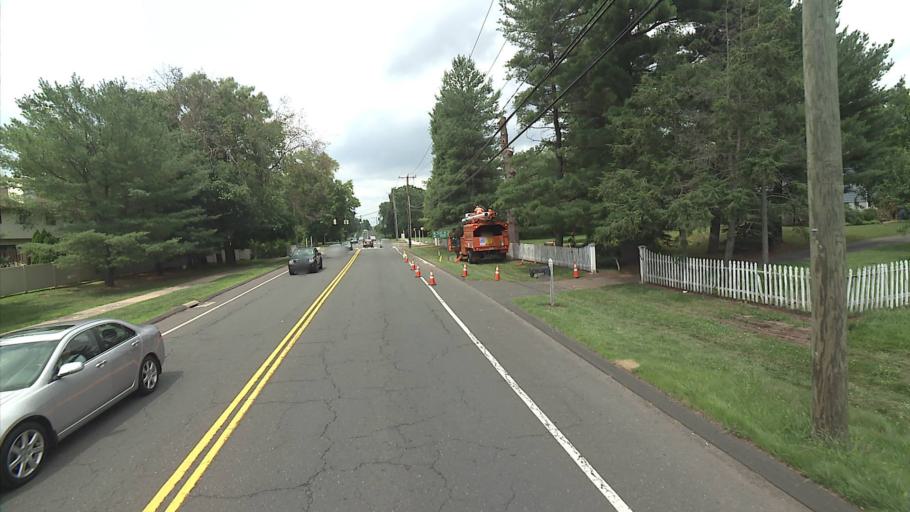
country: US
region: Connecticut
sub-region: Hartford County
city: Newington
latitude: 41.6703
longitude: -72.7282
